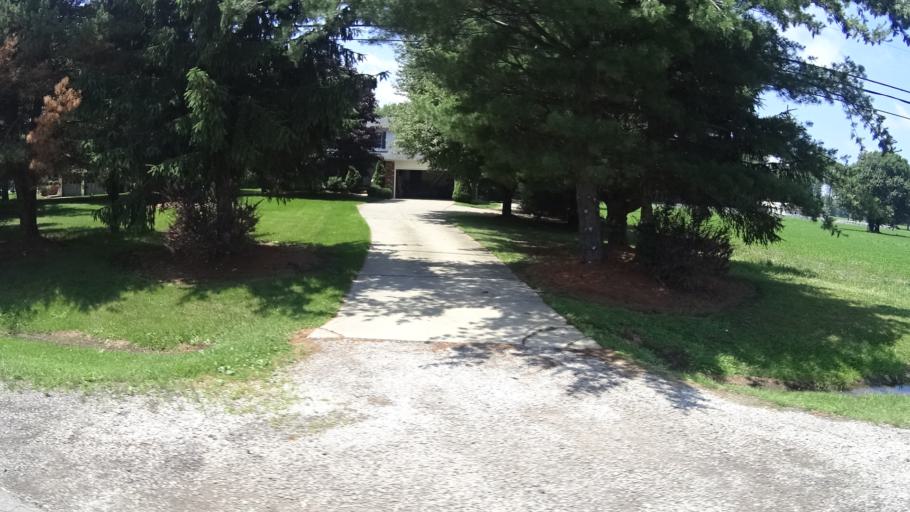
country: US
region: Ohio
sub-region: Lorain County
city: Vermilion
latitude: 41.3578
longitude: -82.3594
